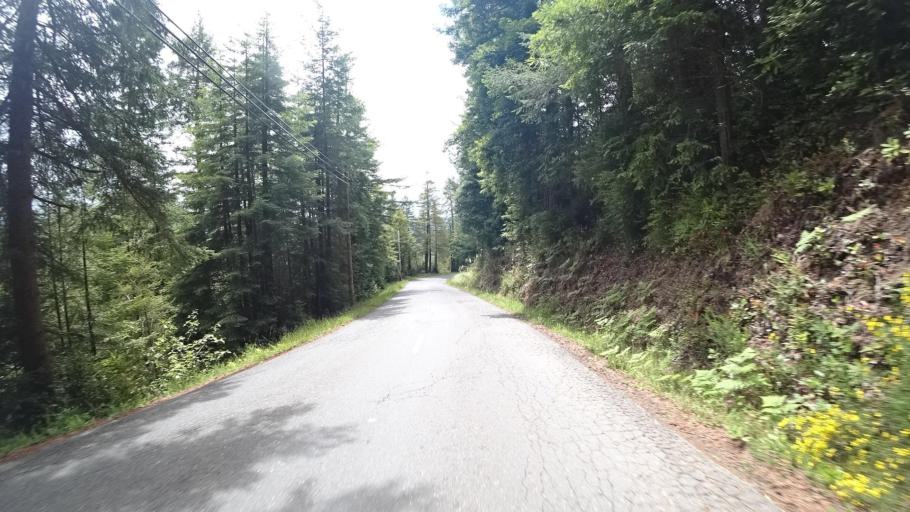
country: US
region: California
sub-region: Humboldt County
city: Bayside
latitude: 40.7861
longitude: -124.0572
